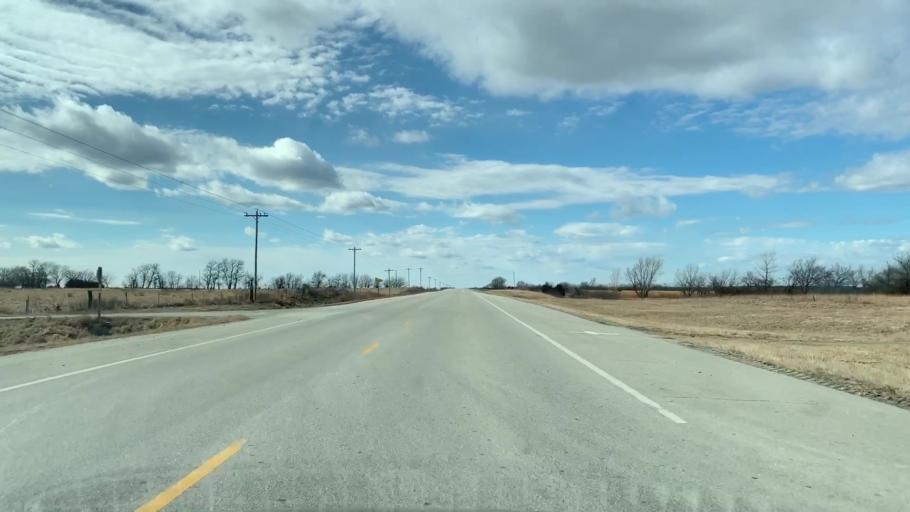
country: US
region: Kansas
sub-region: Neosho County
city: Erie
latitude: 37.5291
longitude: -95.3791
